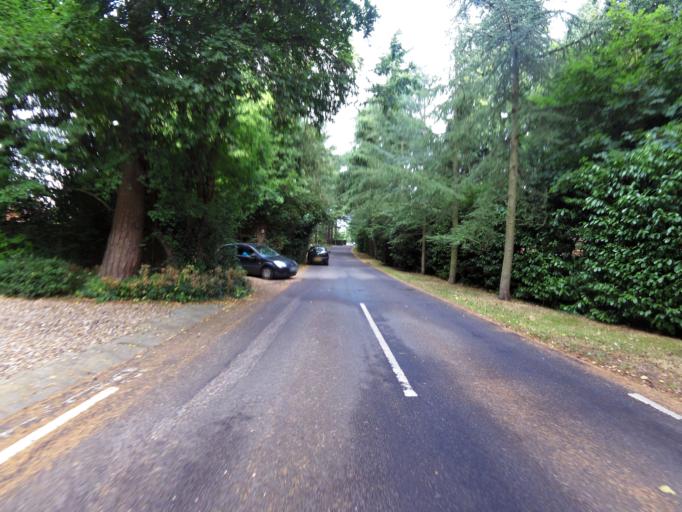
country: GB
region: England
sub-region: Hertfordshire
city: Radlett
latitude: 51.6885
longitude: -0.3127
